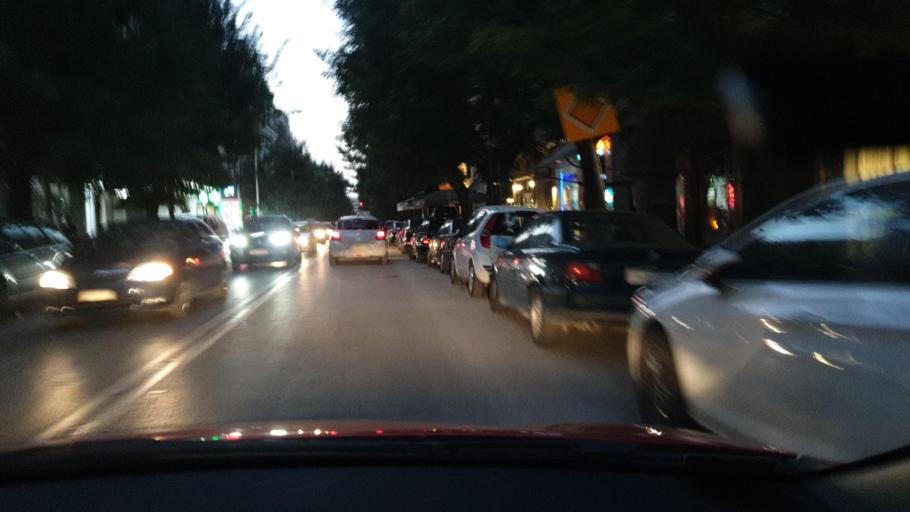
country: GR
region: Central Macedonia
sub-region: Nomos Thessalonikis
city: Triandria
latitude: 40.6072
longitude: 22.9577
